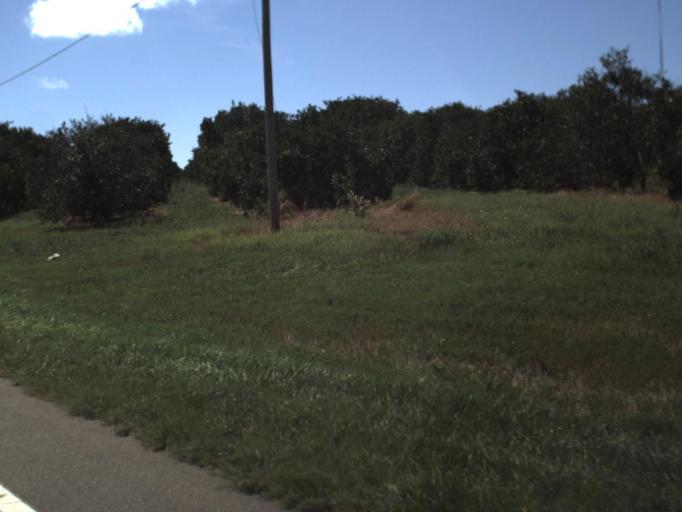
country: US
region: Florida
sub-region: Polk County
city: Frostproof
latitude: 27.7731
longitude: -81.5353
